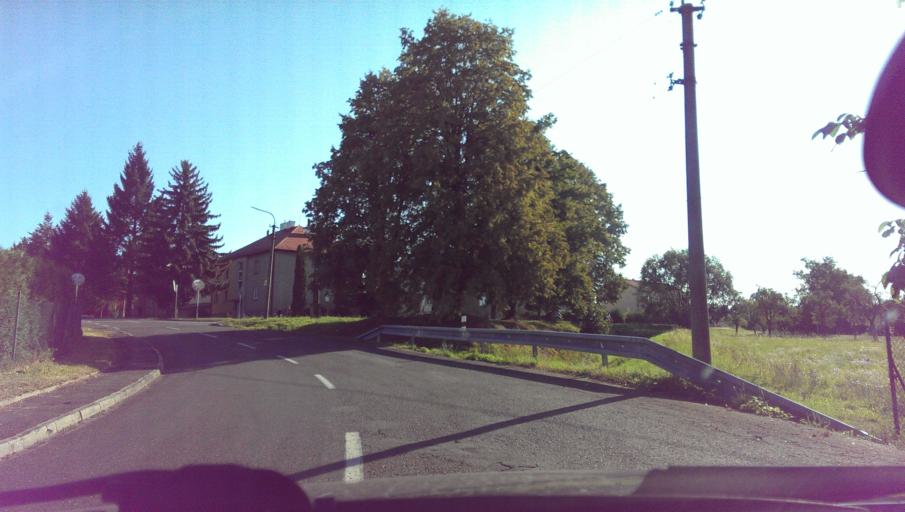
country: CZ
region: Olomoucky
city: Hustopece Nad Becvou
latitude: 49.5332
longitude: 17.8721
